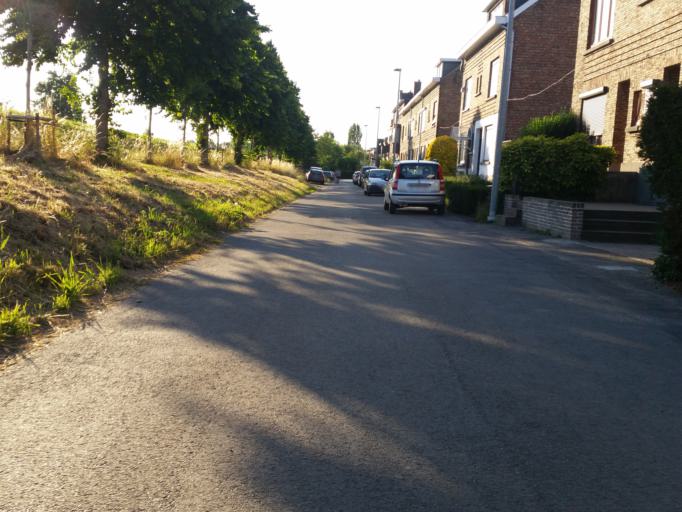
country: BE
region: Flanders
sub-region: Provincie Antwerpen
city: Mechelen
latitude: 51.0283
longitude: 4.4620
